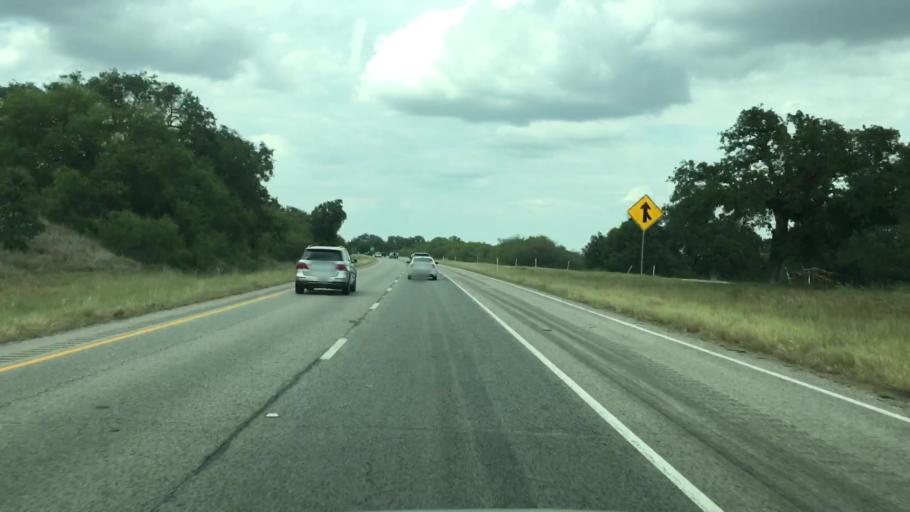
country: US
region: Texas
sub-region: Atascosa County
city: Pleasanton
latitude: 29.0370
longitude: -98.4318
